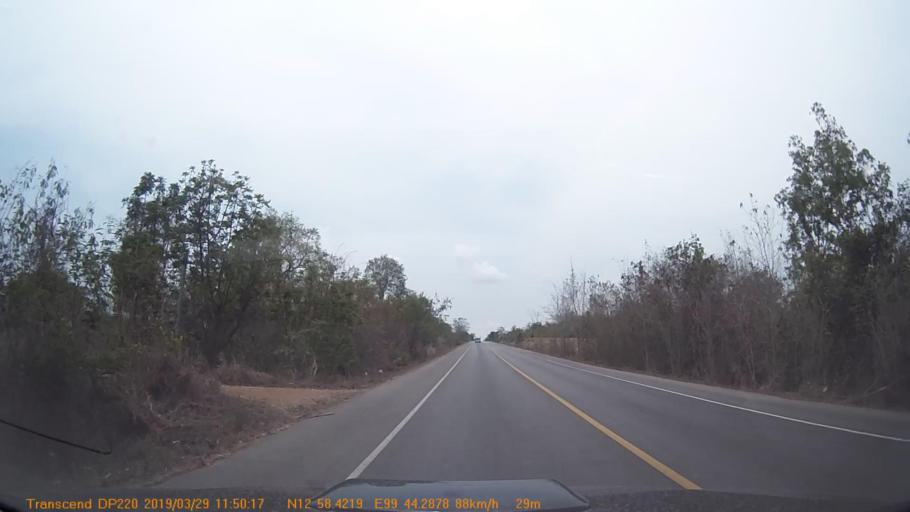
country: TH
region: Phetchaburi
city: Kaeng Krachan
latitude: 12.9736
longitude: 99.7382
